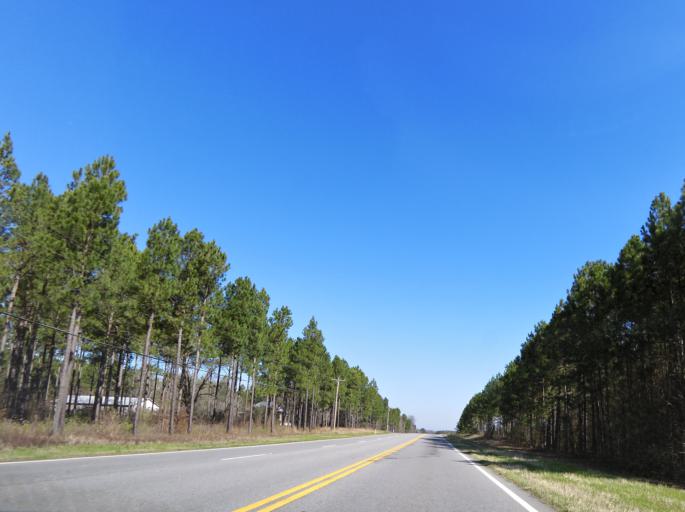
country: US
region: Georgia
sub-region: Pulaski County
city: Hawkinsville
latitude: 32.3145
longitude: -83.4196
